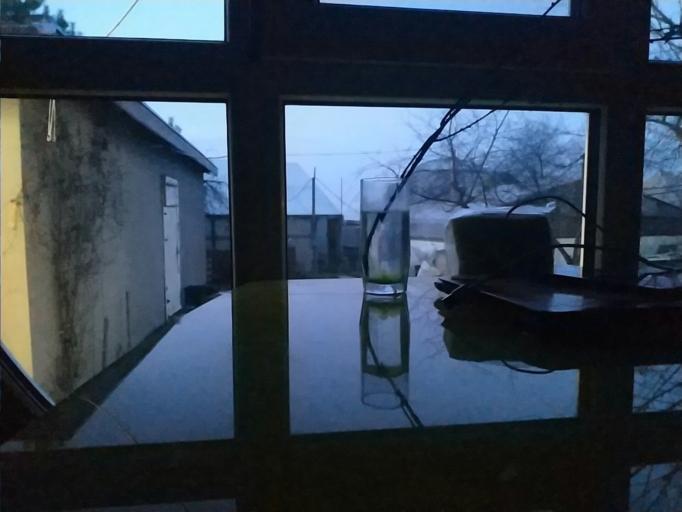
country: RU
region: Republic of Karelia
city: Sukkozero
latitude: 62.8671
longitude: 31.8134
